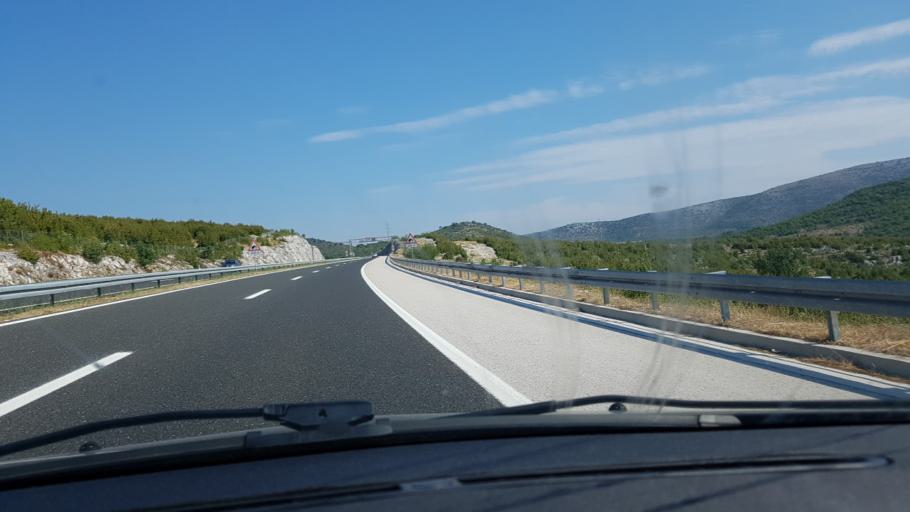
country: HR
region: Splitsko-Dalmatinska
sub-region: Grad Trogir
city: Trogir
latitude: 43.6477
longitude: 16.1998
